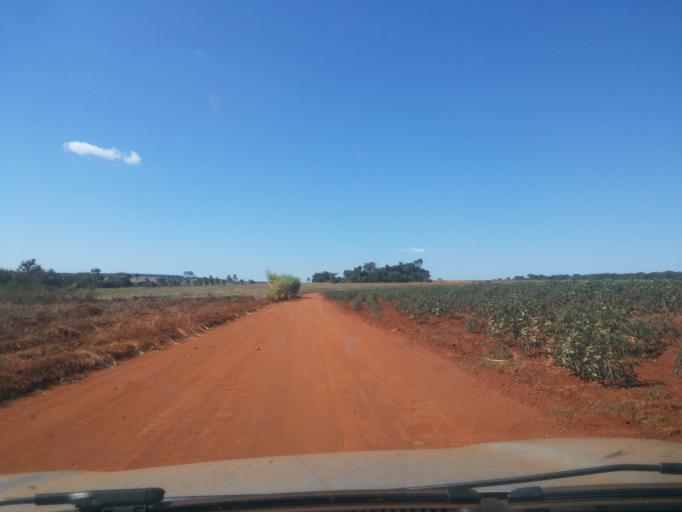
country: BR
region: Minas Gerais
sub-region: Centralina
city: Centralina
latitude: -18.7396
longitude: -49.1949
